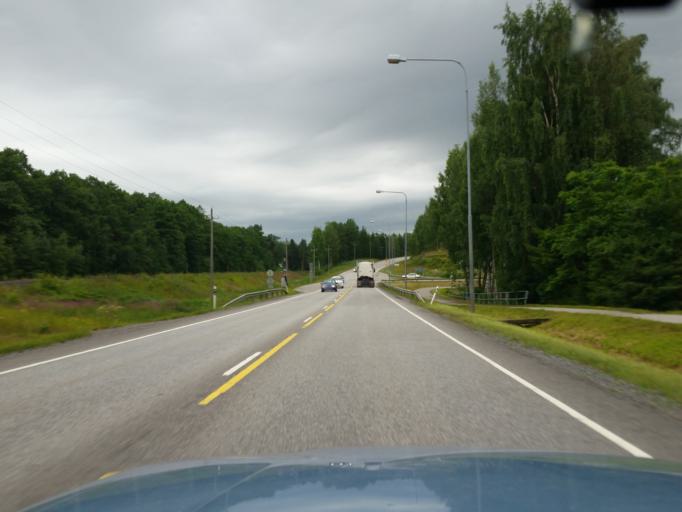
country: FI
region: Uusimaa
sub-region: Raaseporin
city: Ekenaes
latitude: 59.9791
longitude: 23.4003
